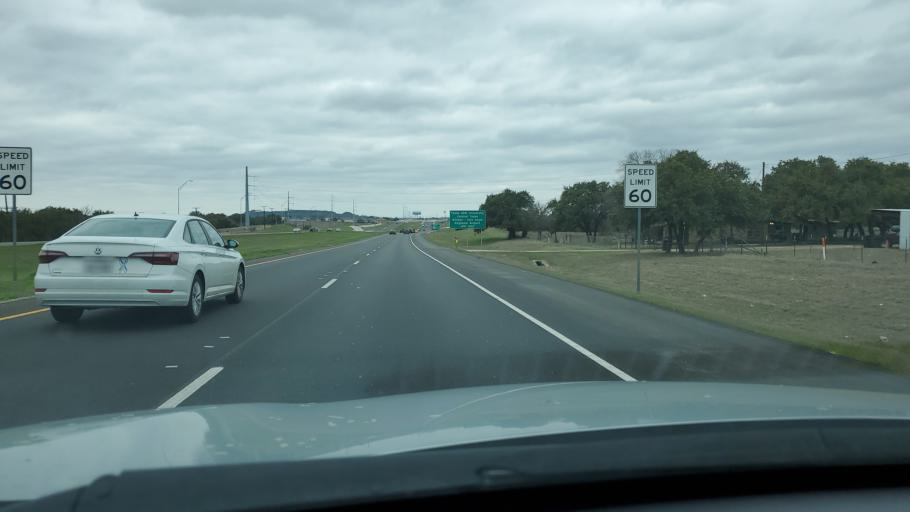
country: US
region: Texas
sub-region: Bell County
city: Killeen
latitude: 31.0495
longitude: -97.7624
